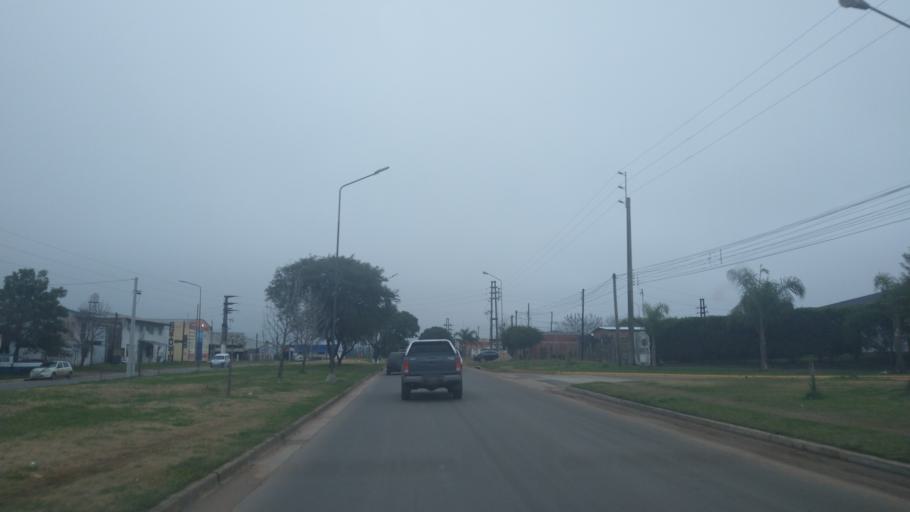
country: AR
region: Entre Rios
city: Chajari
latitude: -30.7615
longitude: -58.0081
